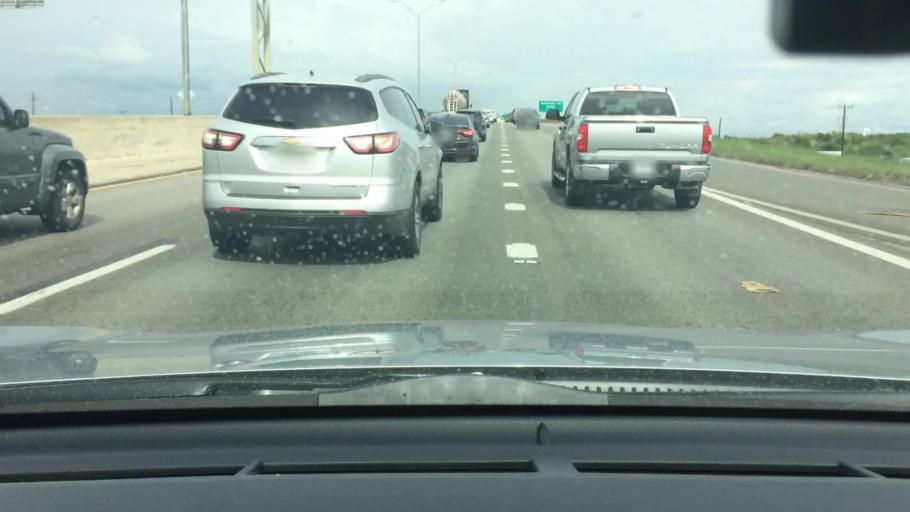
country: US
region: Texas
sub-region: Bexar County
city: Kirby
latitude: 29.4315
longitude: -98.4030
